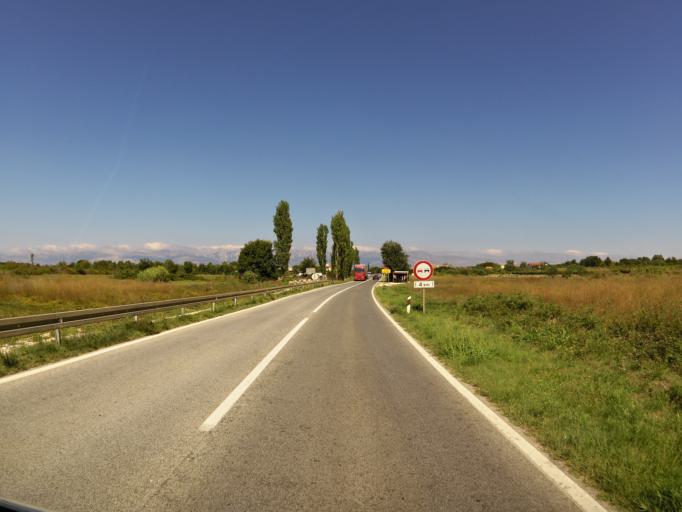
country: HR
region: Zadarska
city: Policnik
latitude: 44.1842
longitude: 15.3944
